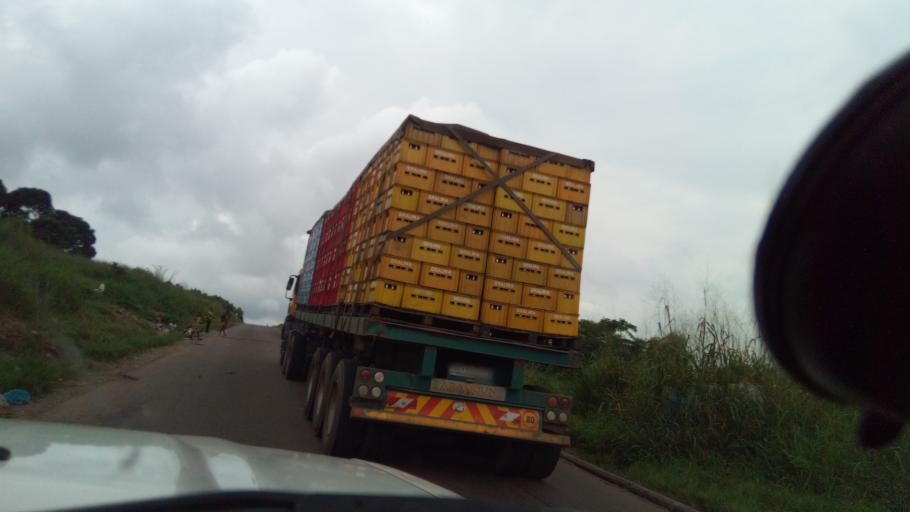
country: CD
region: Bas-Congo
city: Kasangulu
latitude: -4.8340
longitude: 15.1850
